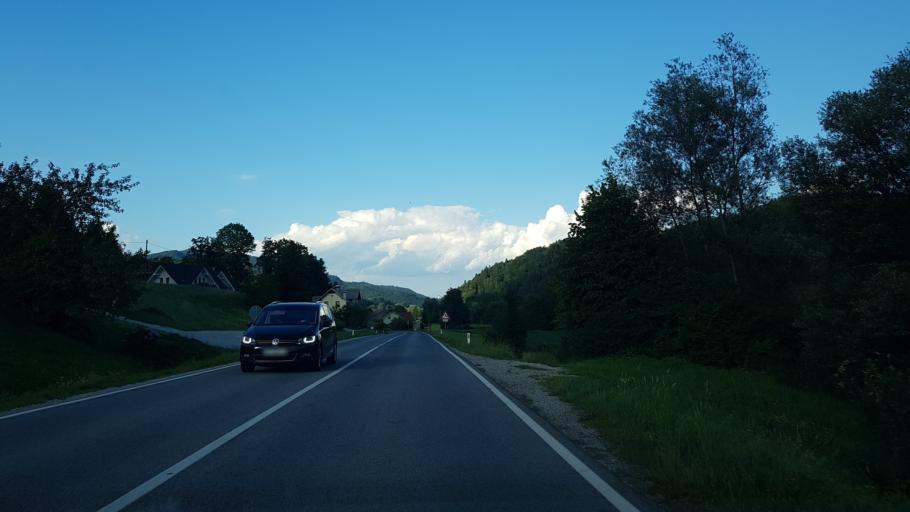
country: SI
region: Gorenja Vas-Poljane
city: Gorenja Vas
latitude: 46.1101
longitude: 14.1543
